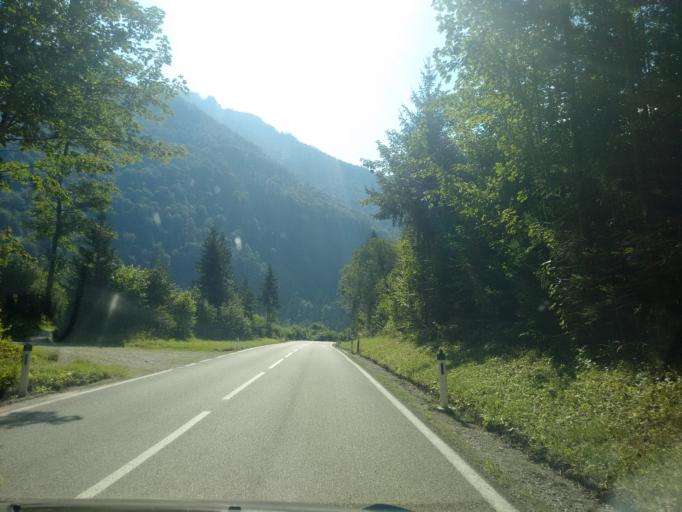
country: AT
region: Upper Austria
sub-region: Politischer Bezirk Gmunden
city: Gruenau im Almtal
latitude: 47.8173
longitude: 13.9517
